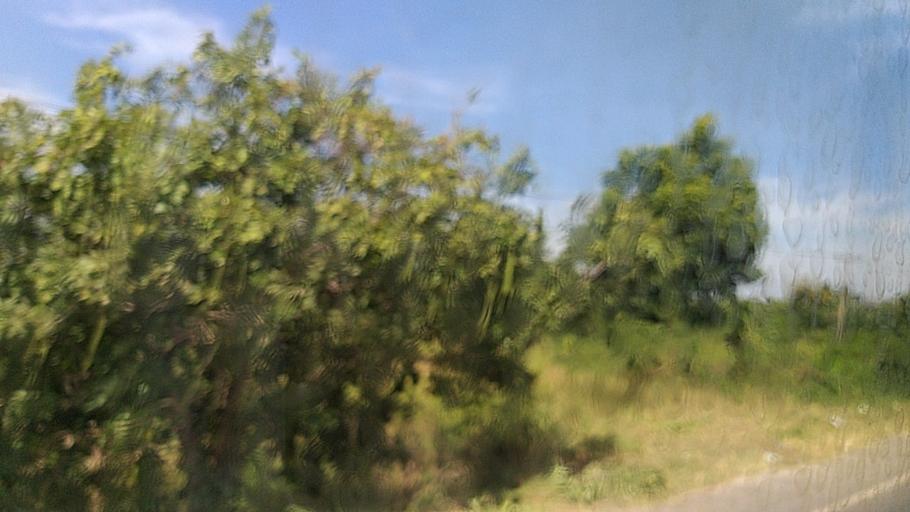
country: TH
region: Khon Kaen
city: Khon Kaen
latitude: 16.4288
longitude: 102.9173
